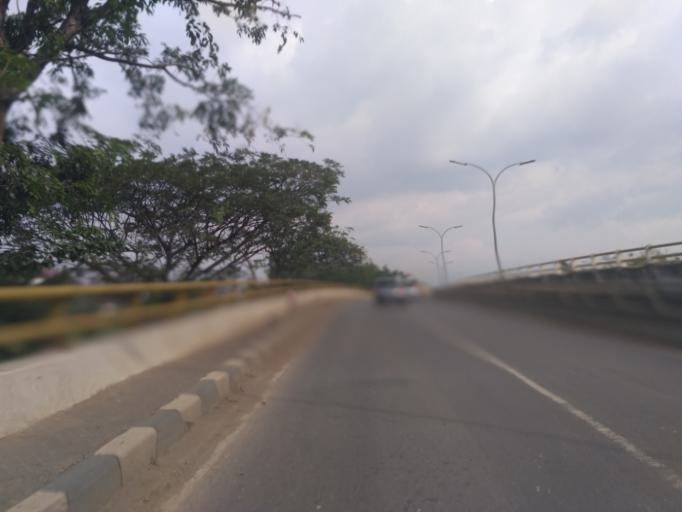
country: ID
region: Central Java
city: Semarang
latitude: -6.9781
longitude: 110.3878
